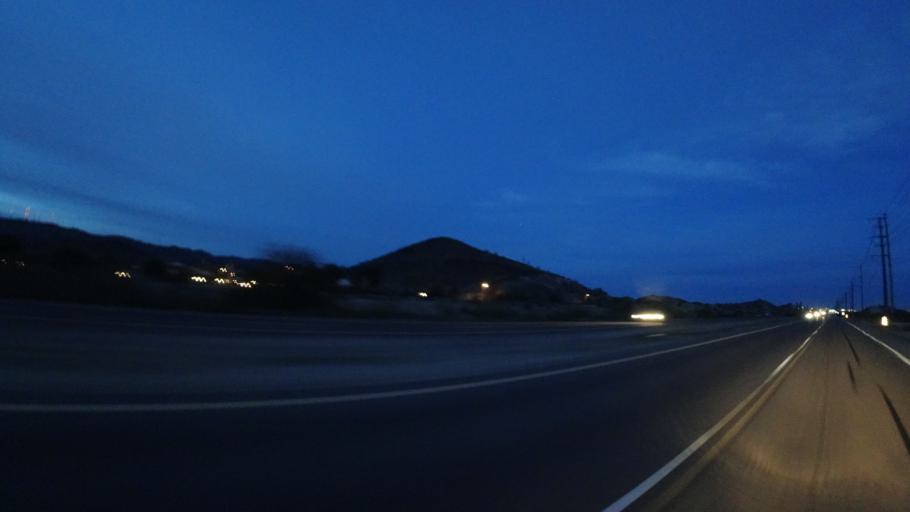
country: US
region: Arizona
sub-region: Maricopa County
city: Guadalupe
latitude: 33.2910
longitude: -112.0442
